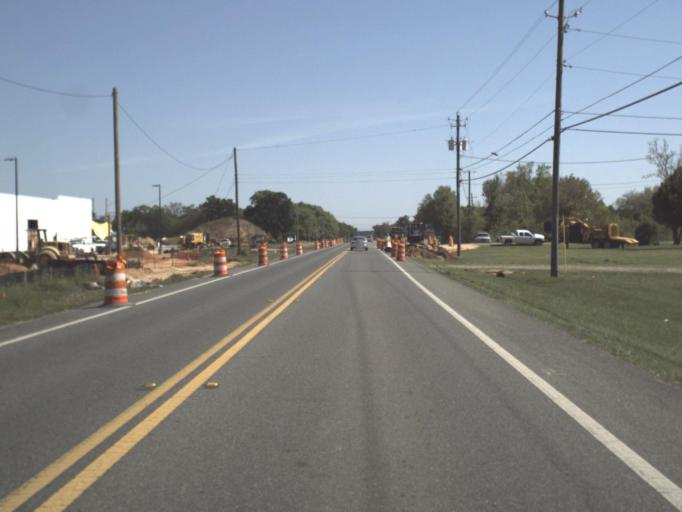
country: US
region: Florida
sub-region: Escambia County
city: Bellview
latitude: 30.4786
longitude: -87.3095
